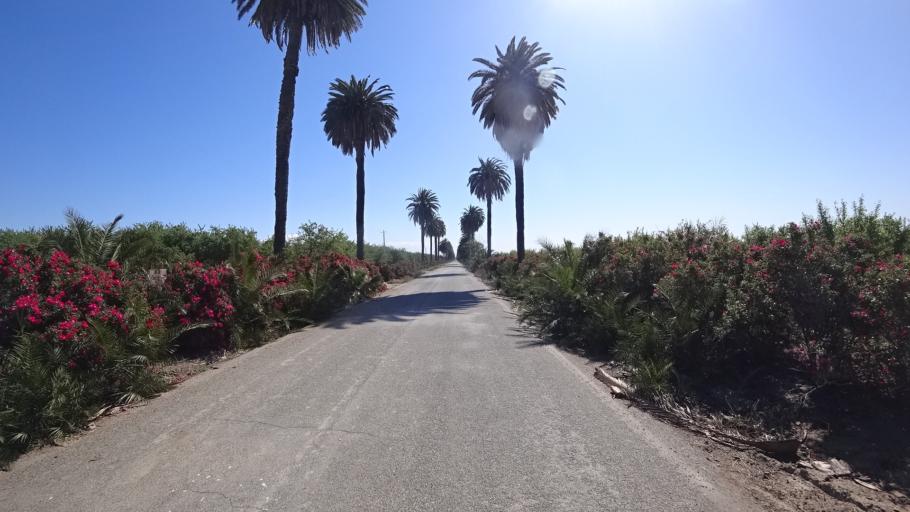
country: US
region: California
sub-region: Glenn County
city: Hamilton City
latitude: 39.7375
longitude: -122.0498
